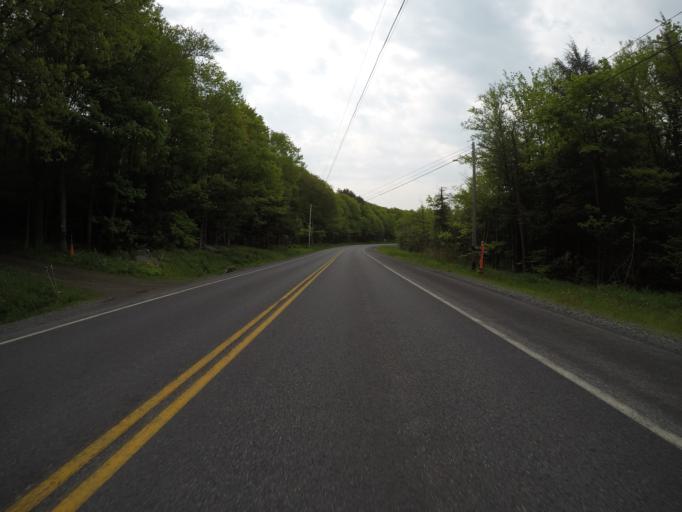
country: US
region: New York
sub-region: Sullivan County
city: Livingston Manor
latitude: 42.0371
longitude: -74.9012
